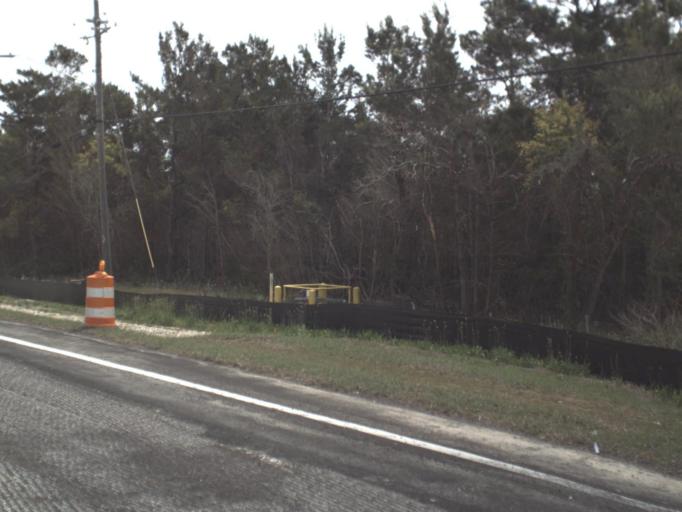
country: US
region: Florida
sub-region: Santa Rosa County
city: Navarre
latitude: 30.4095
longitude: -86.8039
